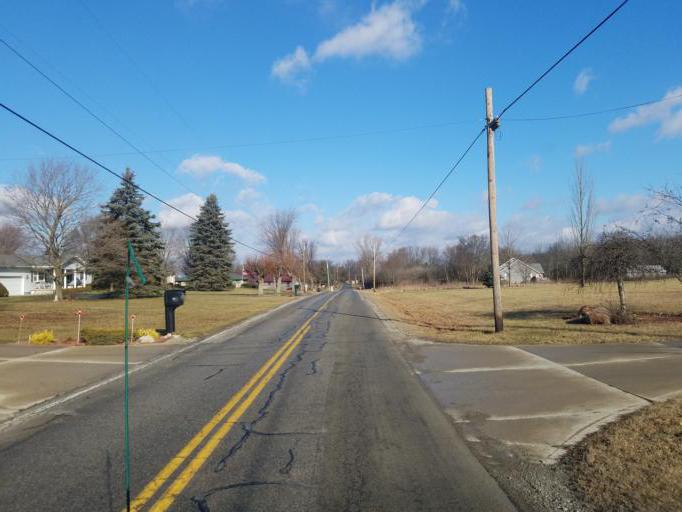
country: US
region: Ohio
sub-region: Marion County
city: Marion
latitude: 40.5604
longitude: -83.1599
